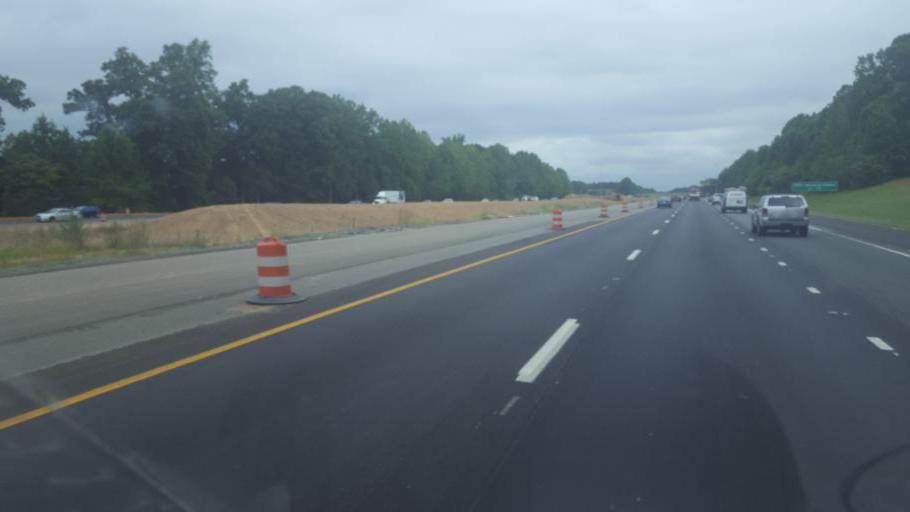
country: US
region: North Carolina
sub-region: Mecklenburg County
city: Huntersville
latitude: 35.4012
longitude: -80.8560
